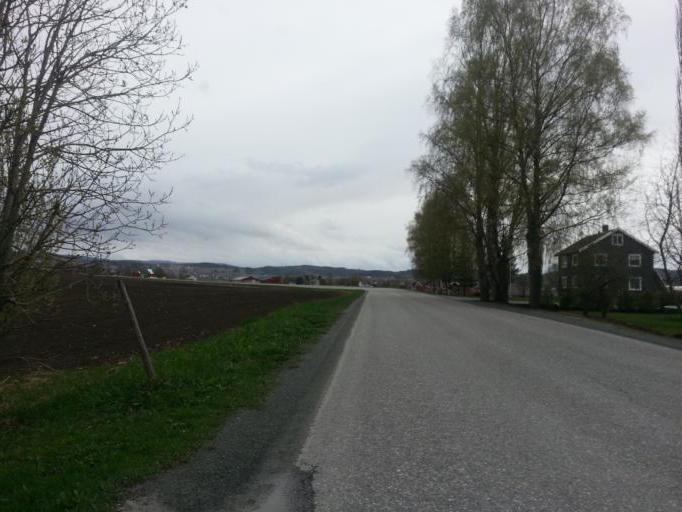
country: NO
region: Nord-Trondelag
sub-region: Levanger
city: Skogn
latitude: 63.6999
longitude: 11.1948
